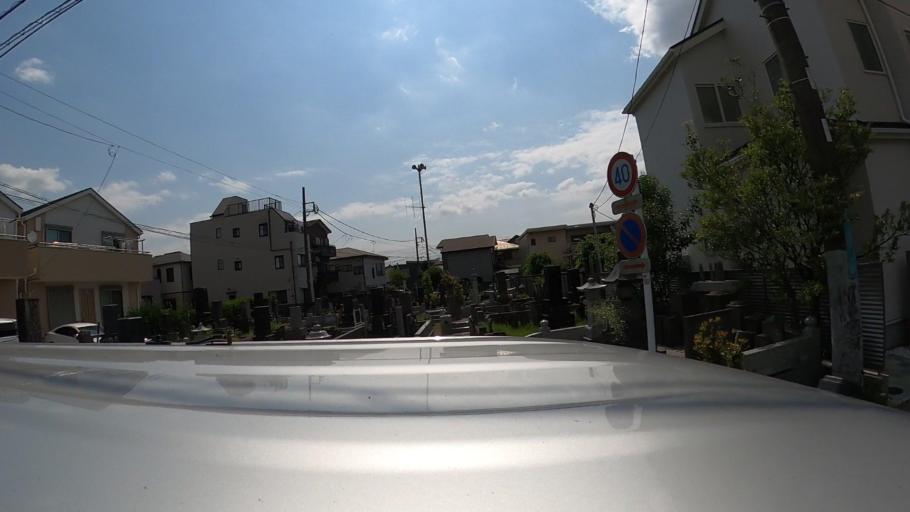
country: JP
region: Kanagawa
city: Chigasaki
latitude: 35.3637
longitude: 139.3880
